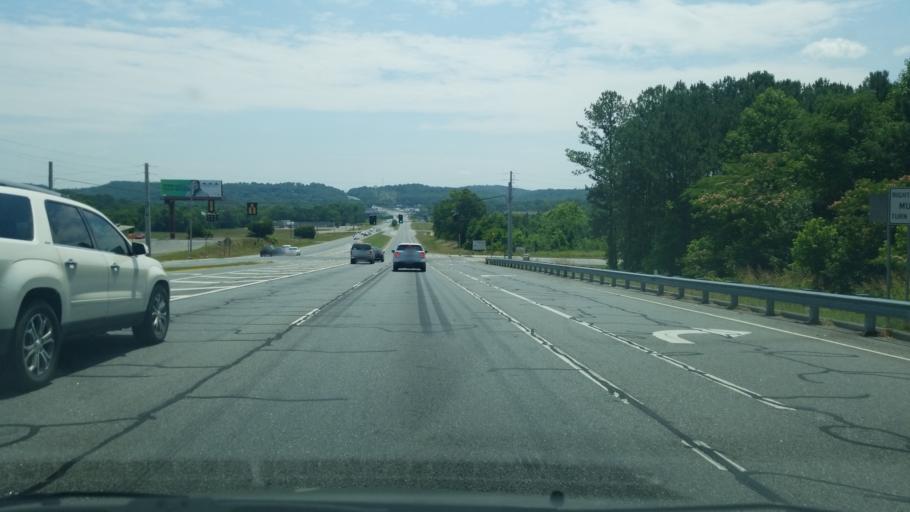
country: US
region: Georgia
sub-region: Catoosa County
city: Indian Springs
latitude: 34.9344
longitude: -85.1936
